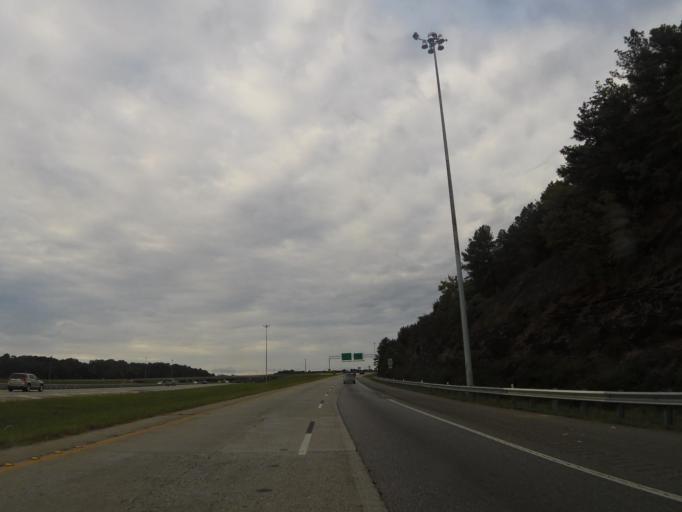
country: US
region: Alabama
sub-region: Jefferson County
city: Hoover
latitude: 33.3886
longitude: -86.7834
